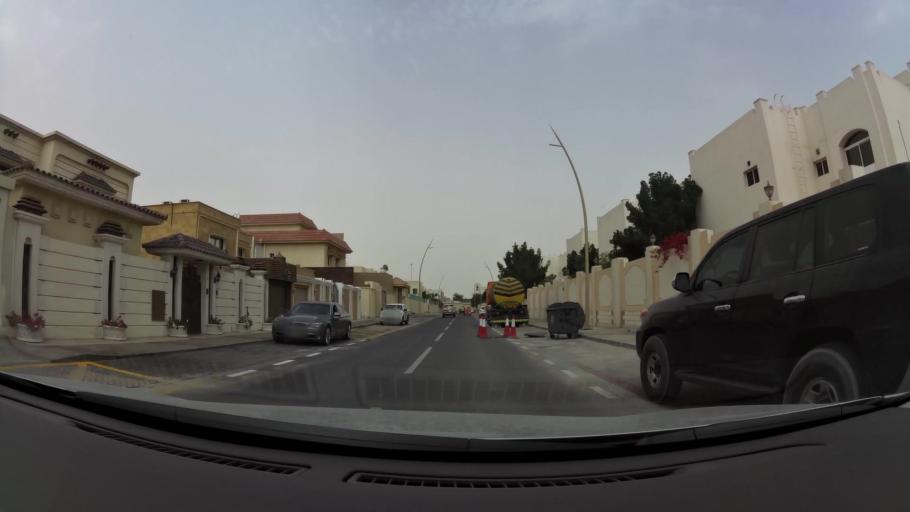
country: QA
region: Baladiyat ad Dawhah
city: Doha
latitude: 25.2628
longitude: 51.5004
